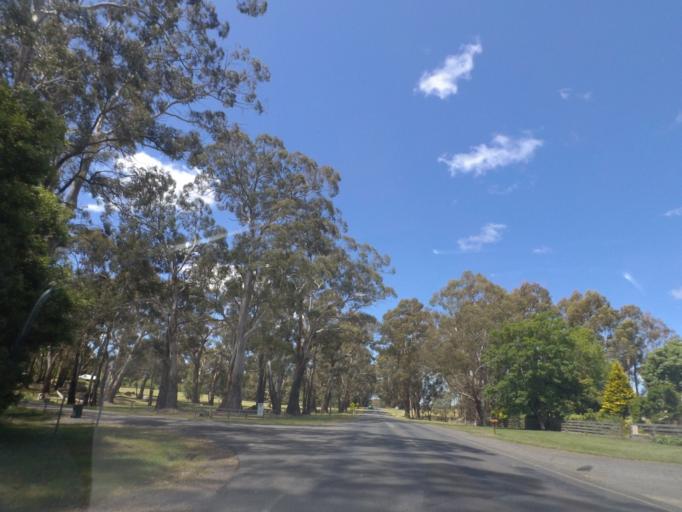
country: AU
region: Victoria
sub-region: Mount Alexander
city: Castlemaine
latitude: -37.3165
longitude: 144.2186
